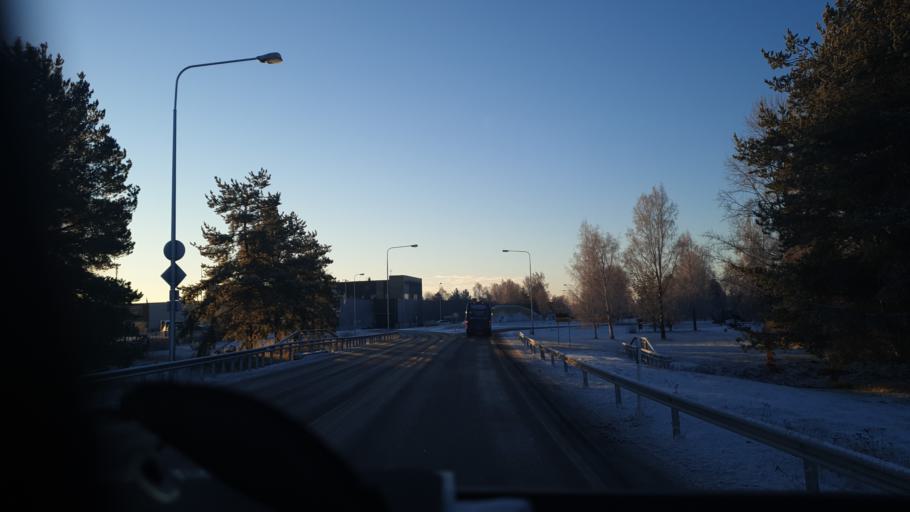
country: FI
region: Northern Ostrobothnia
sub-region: Ylivieska
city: Kalajoki
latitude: 64.2620
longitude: 23.9483
